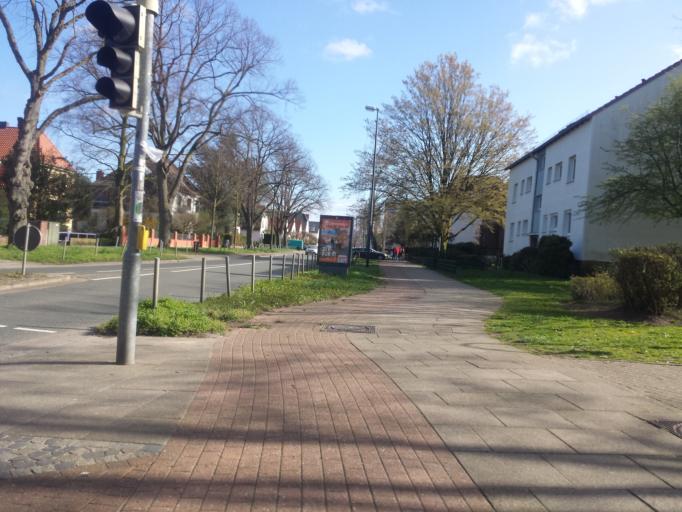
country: DE
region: Lower Saxony
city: Lilienthal
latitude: 53.0649
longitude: 8.8891
